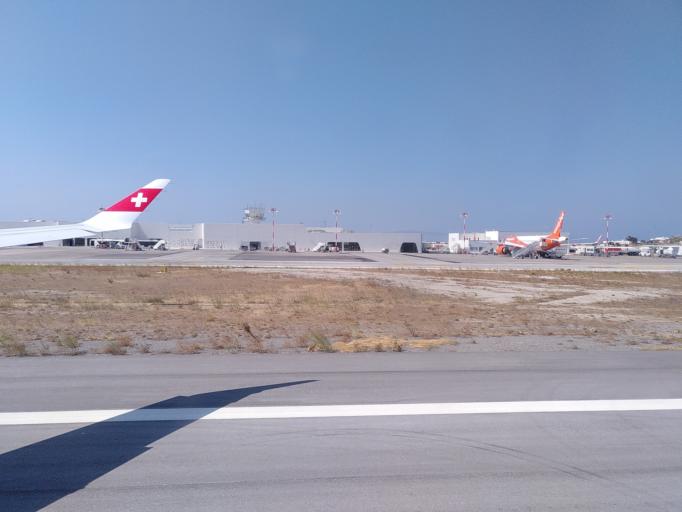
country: GR
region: South Aegean
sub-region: Nomos Kykladon
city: Mykonos
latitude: 37.4358
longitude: 25.3481
